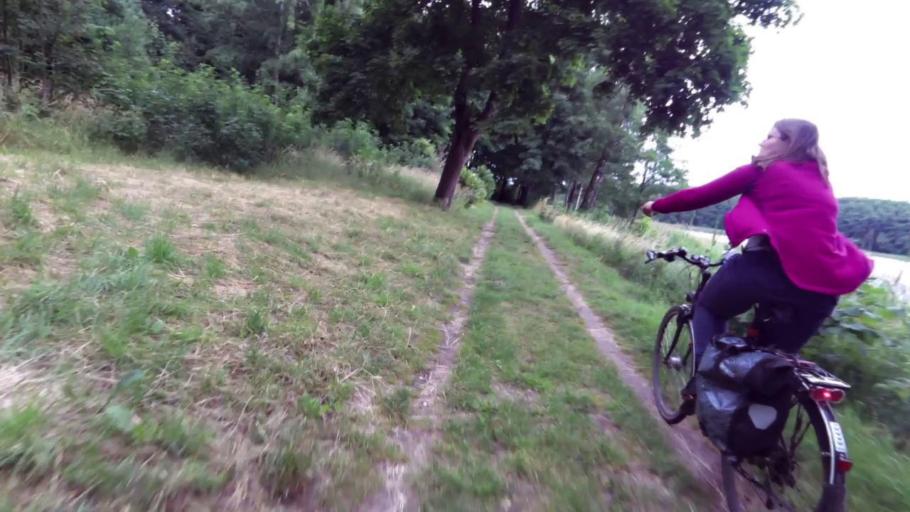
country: PL
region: West Pomeranian Voivodeship
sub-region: Powiat stargardzki
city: Chociwel
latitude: 53.4621
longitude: 15.3454
